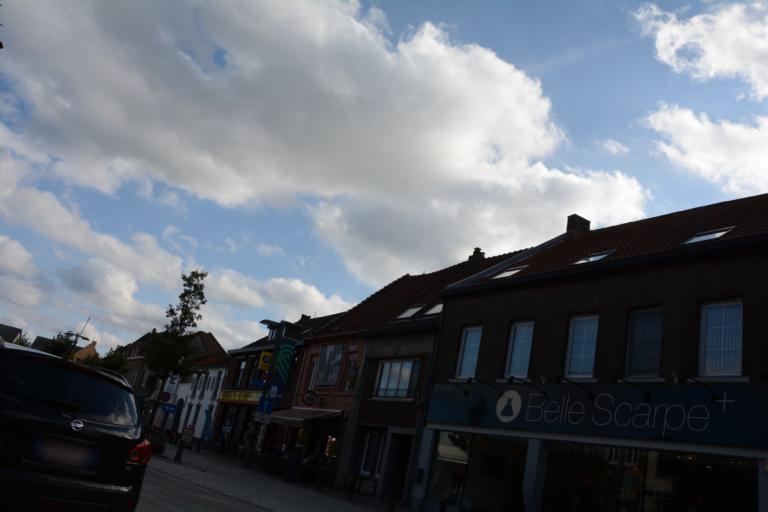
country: BE
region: Flanders
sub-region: Provincie Limburg
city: Peer
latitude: 51.1329
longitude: 5.4537
